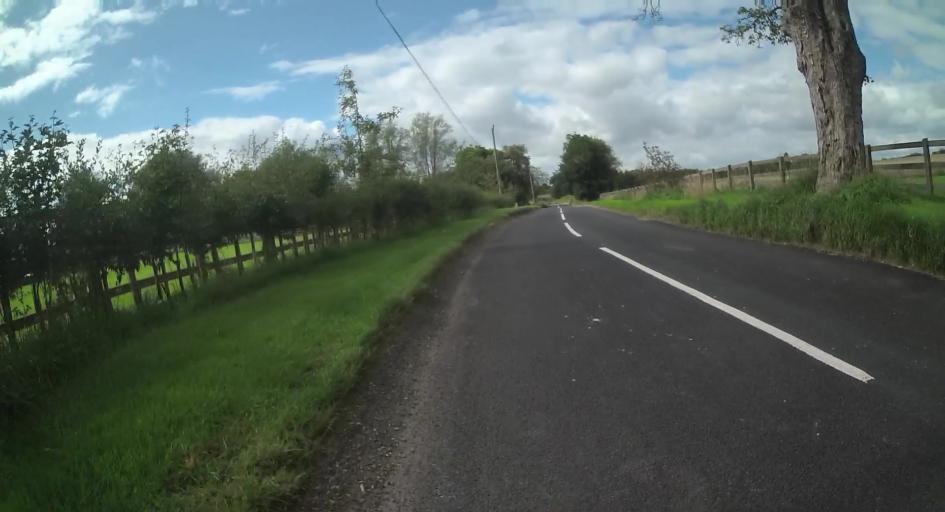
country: GB
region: England
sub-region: Hampshire
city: Overton
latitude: 51.2019
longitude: -1.1746
